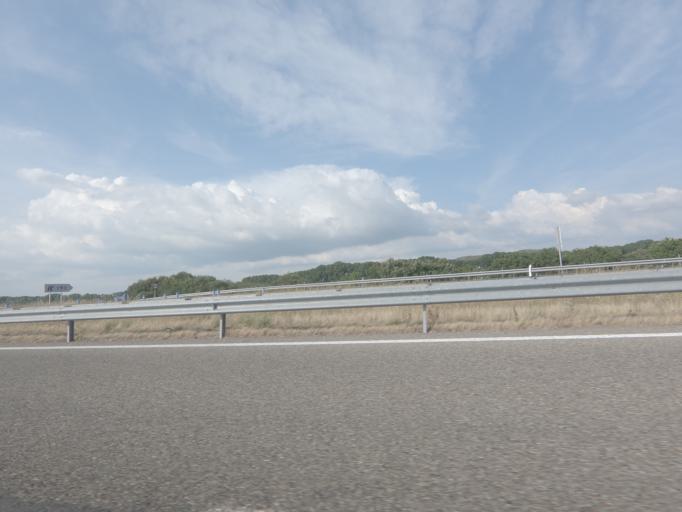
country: ES
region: Galicia
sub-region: Provincia de Ourense
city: Xinzo de Limia
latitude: 42.0777
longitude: -7.7105
